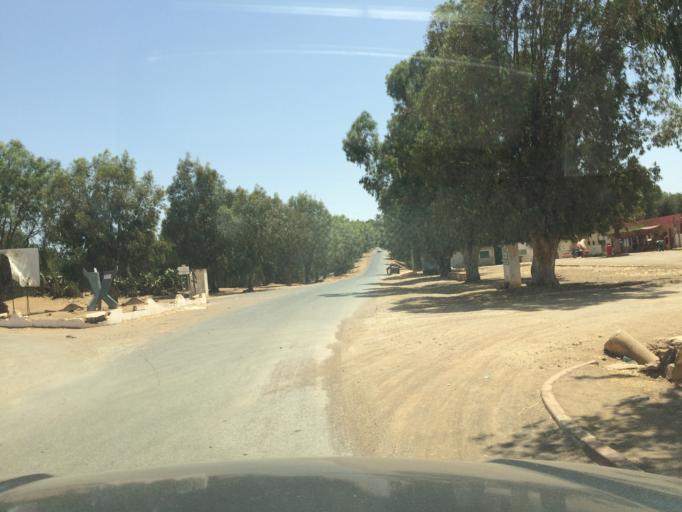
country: MA
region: Chaouia-Ouardigha
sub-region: Benslimane
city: Mellila
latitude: 33.5686
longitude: -6.8871
